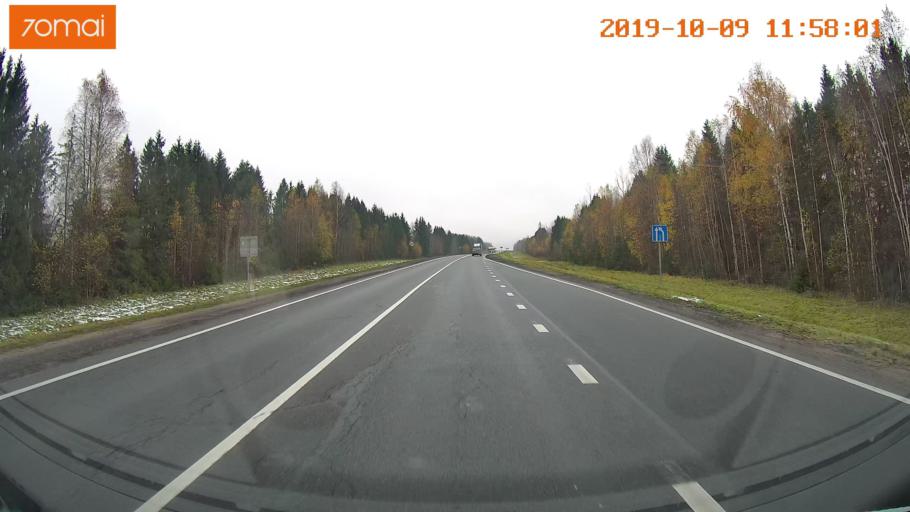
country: RU
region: Vologda
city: Gryazovets
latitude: 58.7240
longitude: 40.2958
